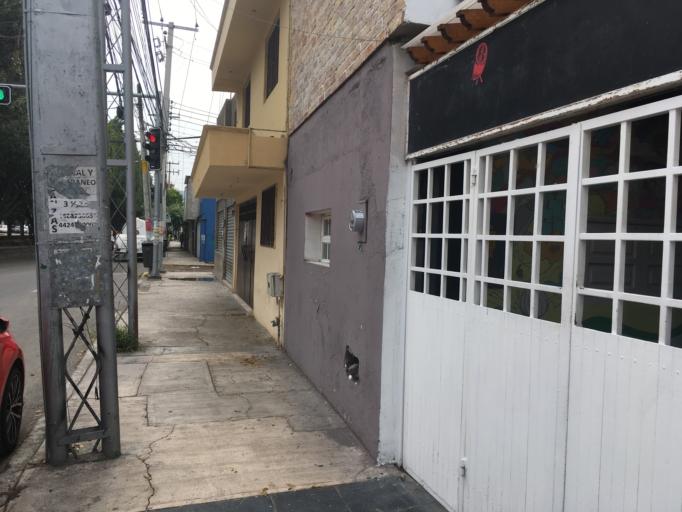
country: MX
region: Queretaro
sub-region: Queretaro
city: Santiago de Queretaro
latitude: 20.6126
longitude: -100.4015
